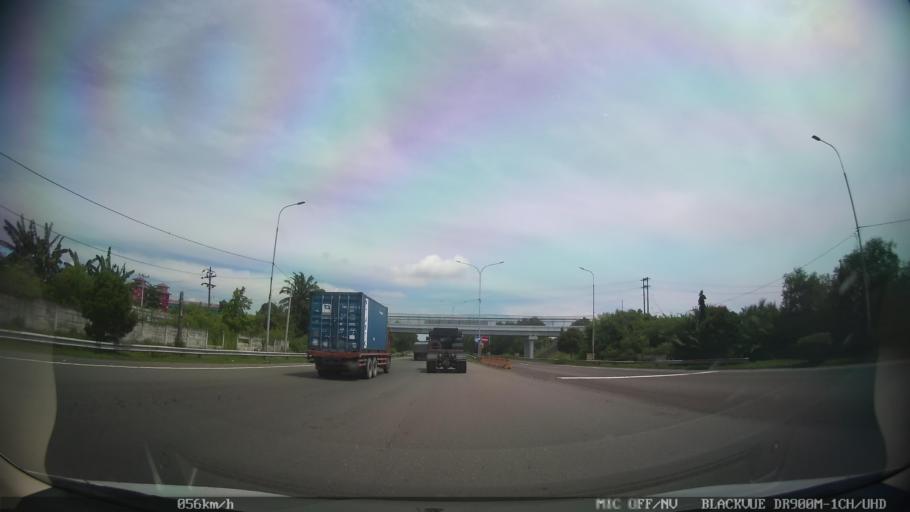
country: ID
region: North Sumatra
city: Labuhan Deli
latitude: 3.7314
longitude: 98.6807
